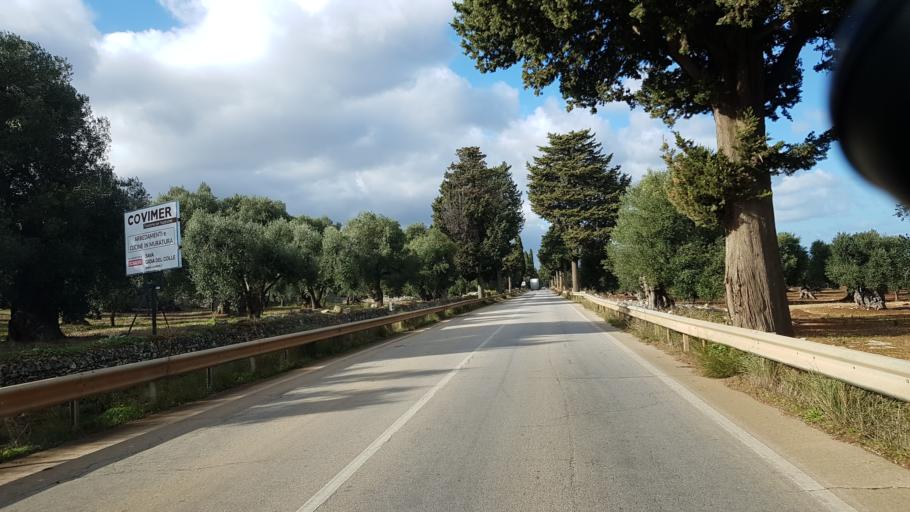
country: IT
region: Apulia
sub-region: Provincia di Brindisi
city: Ostuni
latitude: 40.7511
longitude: 17.5499
